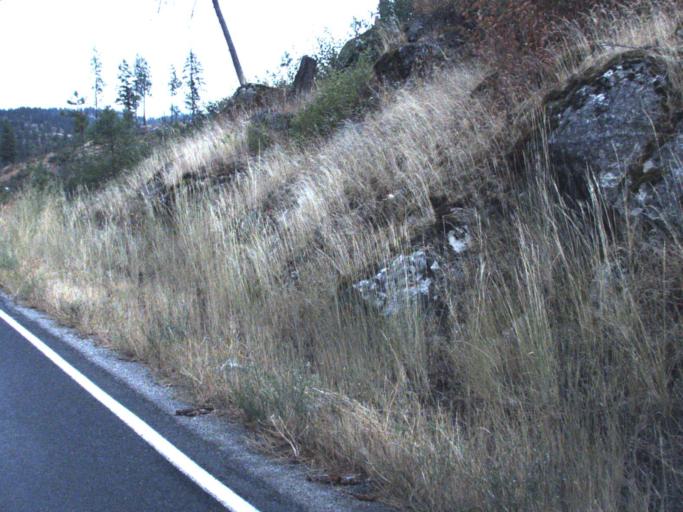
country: US
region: Washington
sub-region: Spokane County
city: Deer Park
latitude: 47.9747
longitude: -117.7341
